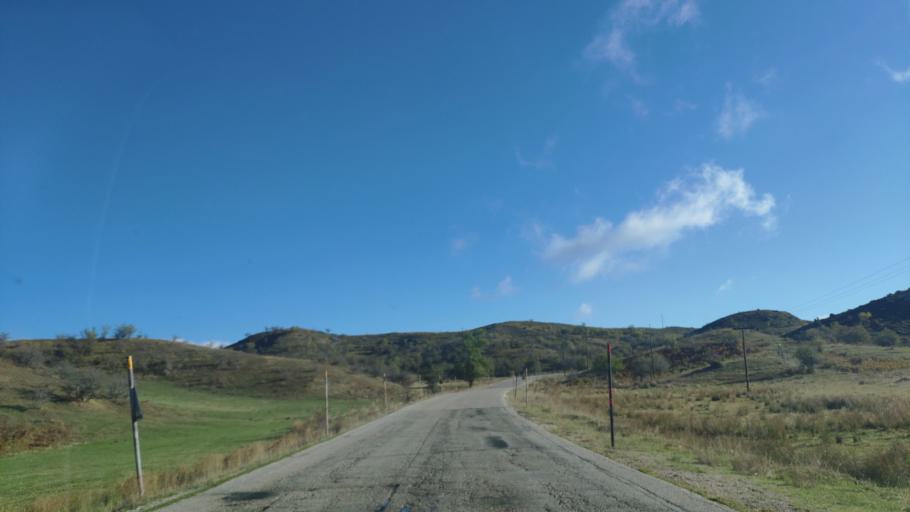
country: GR
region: Epirus
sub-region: Nomos Ioanninon
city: Metsovo
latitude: 39.7882
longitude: 21.1595
